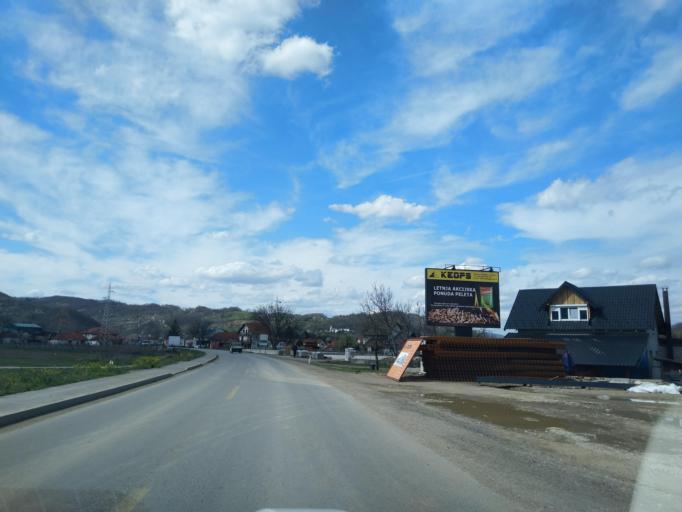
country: RS
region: Central Serbia
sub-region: Zlatiborski Okrug
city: Arilje
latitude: 43.7541
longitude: 20.1038
